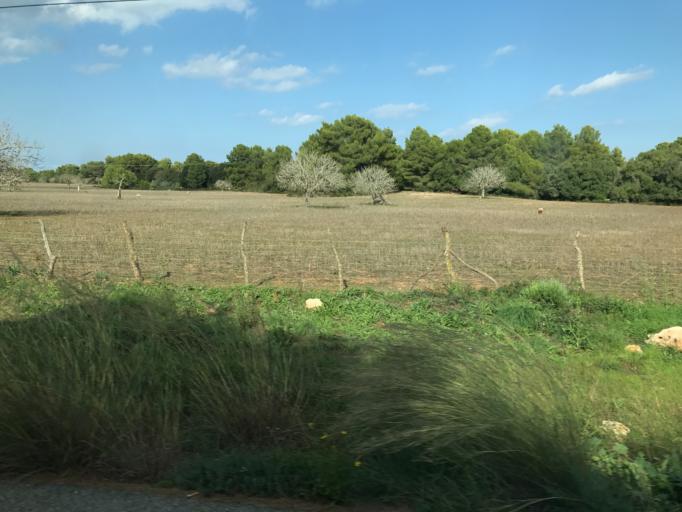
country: ES
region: Balearic Islands
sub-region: Illes Balears
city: Santa Margalida
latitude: 39.7320
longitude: 3.1882
